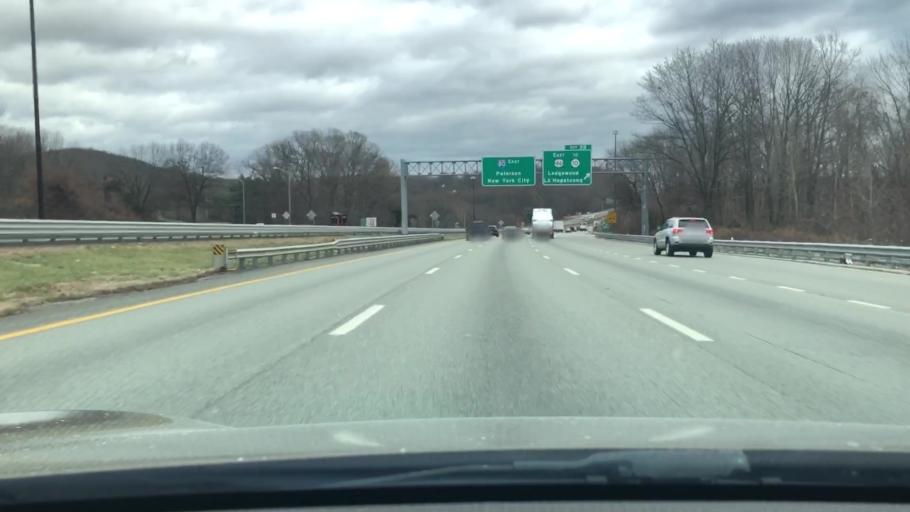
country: US
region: New Jersey
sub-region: Morris County
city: Netcong
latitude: 40.8925
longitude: -74.6715
